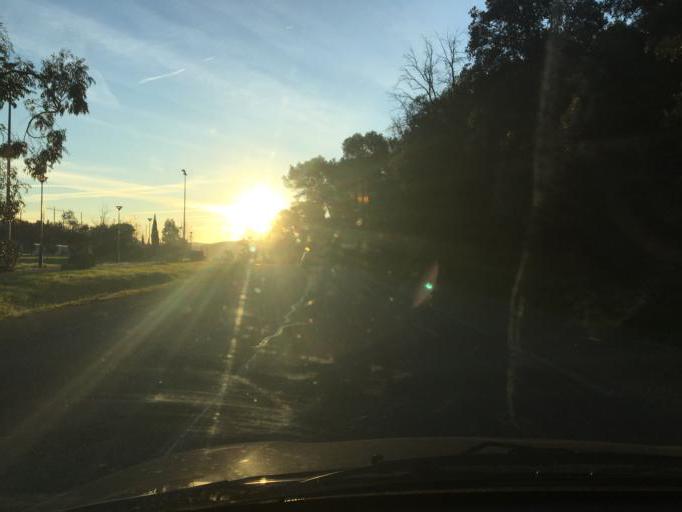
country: FR
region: Provence-Alpes-Cote d'Azur
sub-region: Departement du Var
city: Taradeau
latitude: 43.4508
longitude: 6.4312
